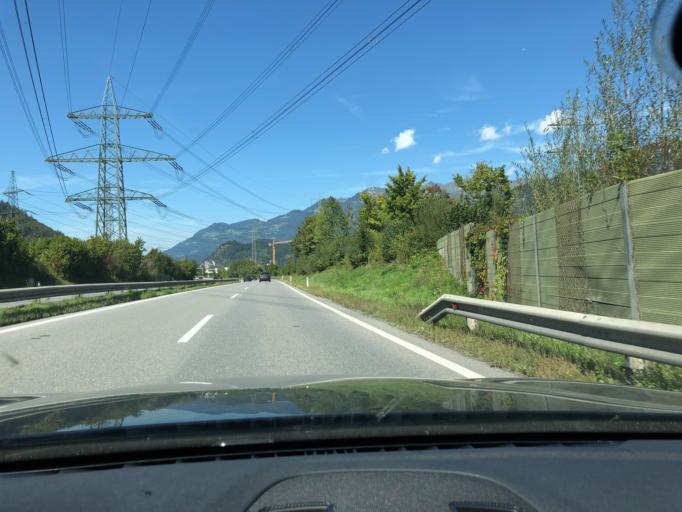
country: AT
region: Vorarlberg
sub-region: Politischer Bezirk Bludenz
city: Buers
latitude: 47.1557
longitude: 9.8077
